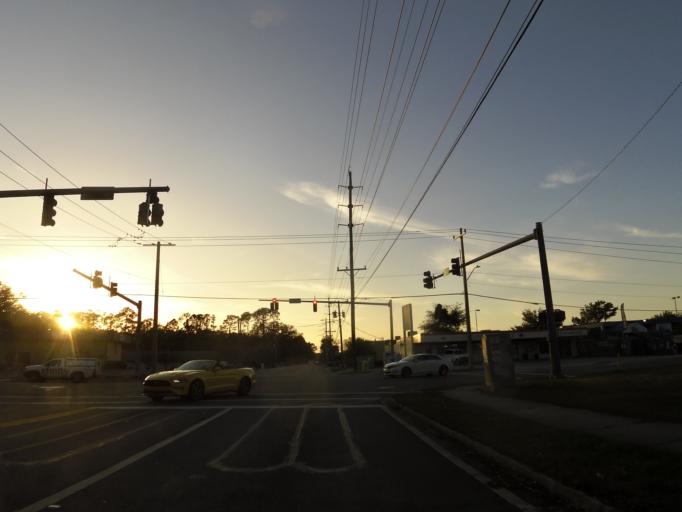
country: US
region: Florida
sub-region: Duval County
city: Jacksonville
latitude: 30.2859
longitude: -81.5789
